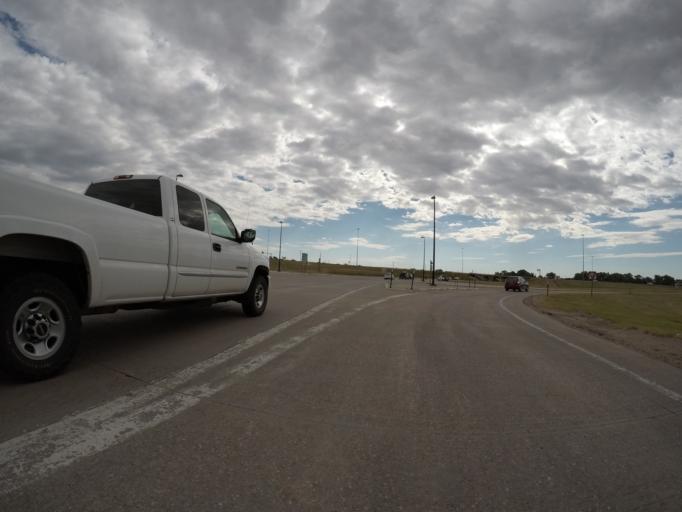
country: US
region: Wyoming
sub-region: Laramie County
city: Cheyenne
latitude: 41.1377
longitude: -104.8441
